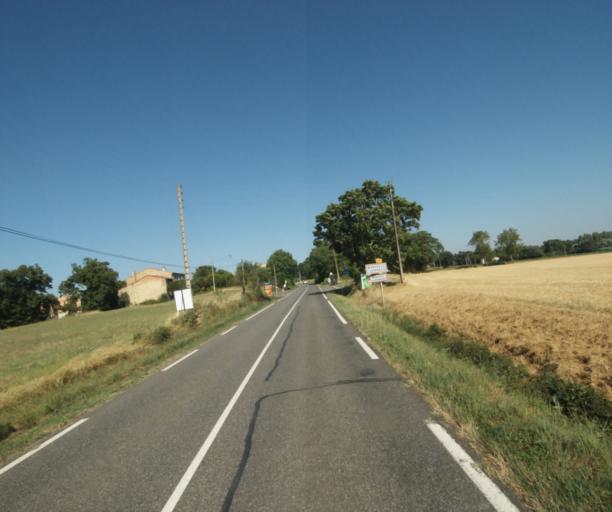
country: FR
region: Midi-Pyrenees
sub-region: Departement de la Haute-Garonne
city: Saint-Felix-Lauragais
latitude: 43.4760
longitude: 1.9298
